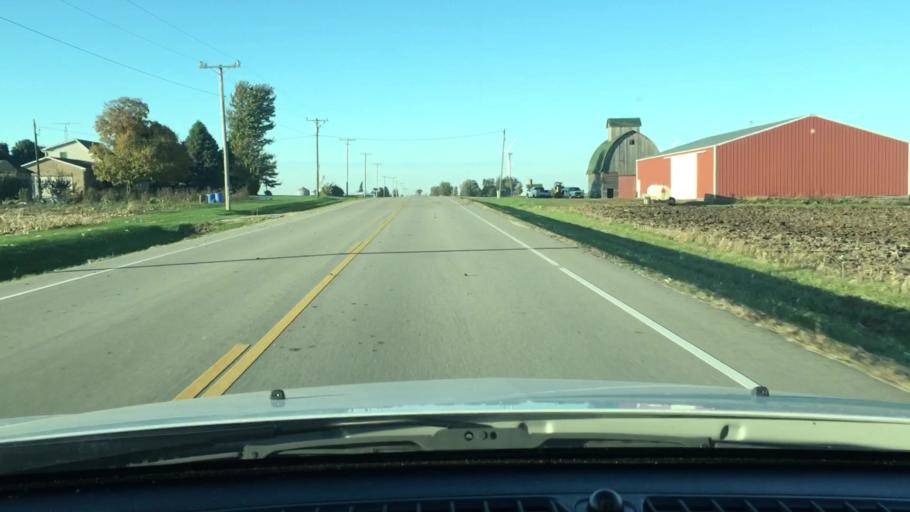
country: US
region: Illinois
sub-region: DeKalb County
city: Malta
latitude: 41.8290
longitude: -88.8864
